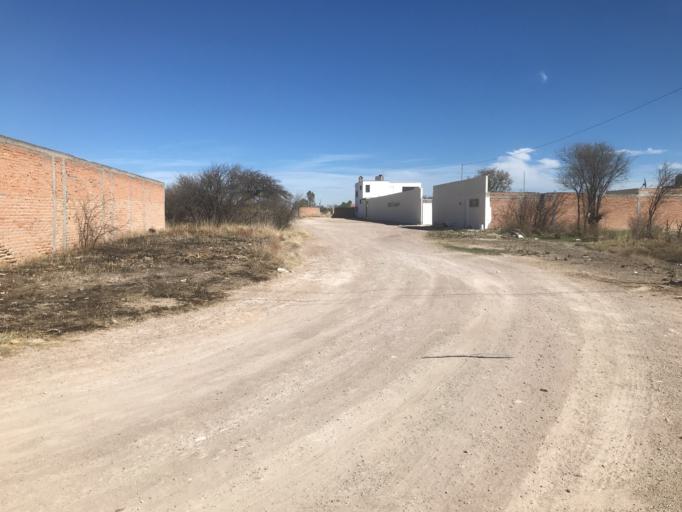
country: MX
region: Durango
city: Victoria de Durango
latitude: 24.0192
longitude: -104.5854
